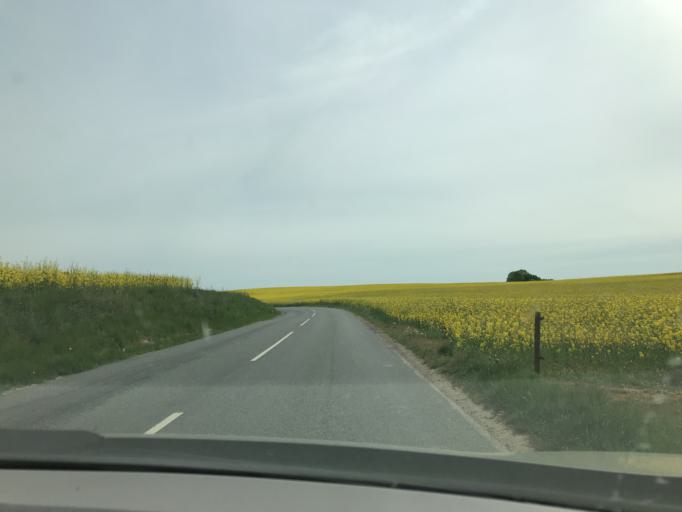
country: DK
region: Central Jutland
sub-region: Norddjurs Kommune
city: Allingabro
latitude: 56.5718
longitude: 10.2966
